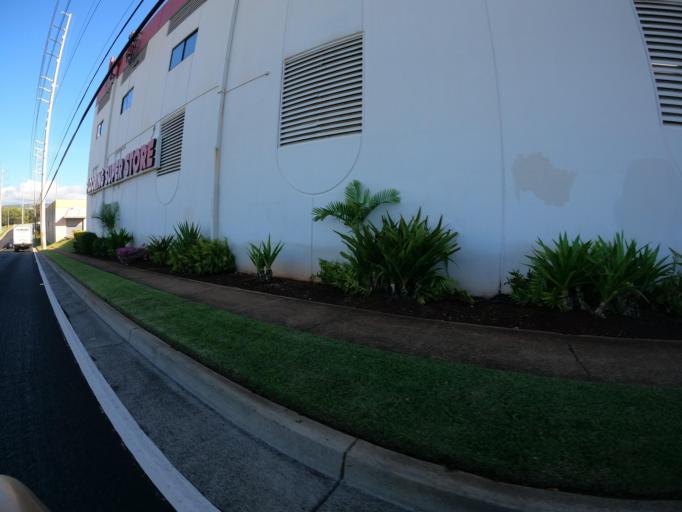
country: US
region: Hawaii
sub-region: Honolulu County
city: Halawa
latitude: 21.3531
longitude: -157.9317
